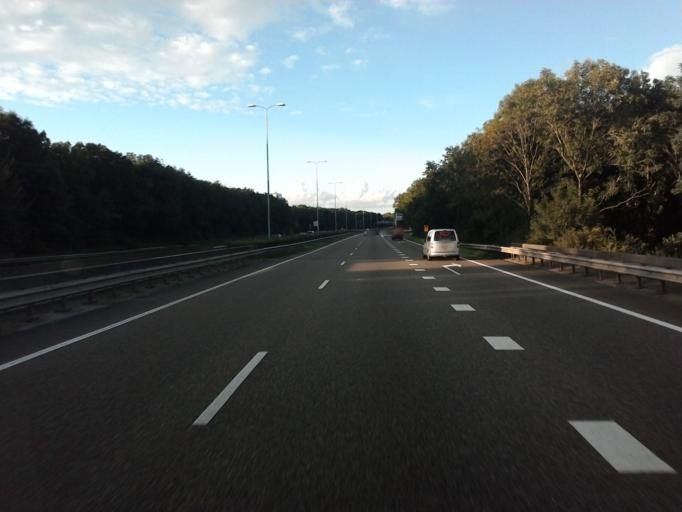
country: NL
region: Utrecht
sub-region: Stichtse Vecht
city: Maarssen
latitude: 52.1211
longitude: 5.0364
